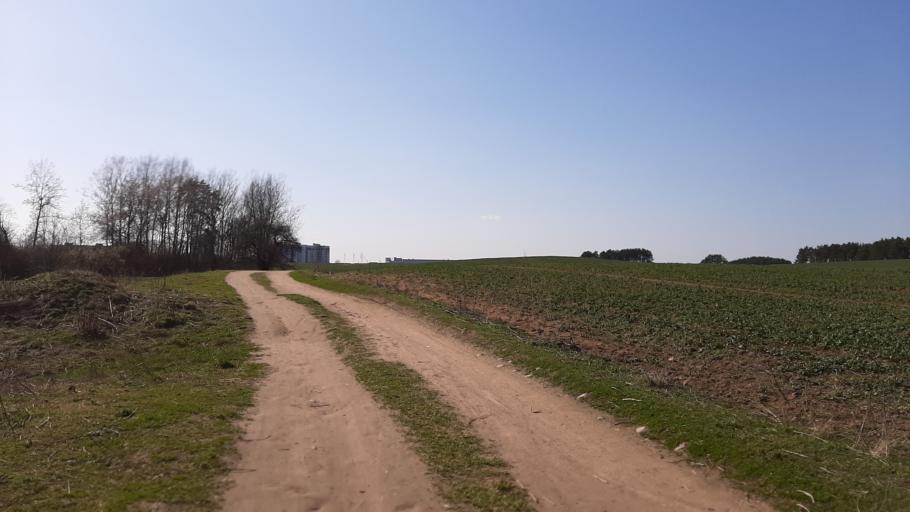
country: BY
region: Minsk
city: Bal'shavik
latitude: 53.9593
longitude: 27.5652
